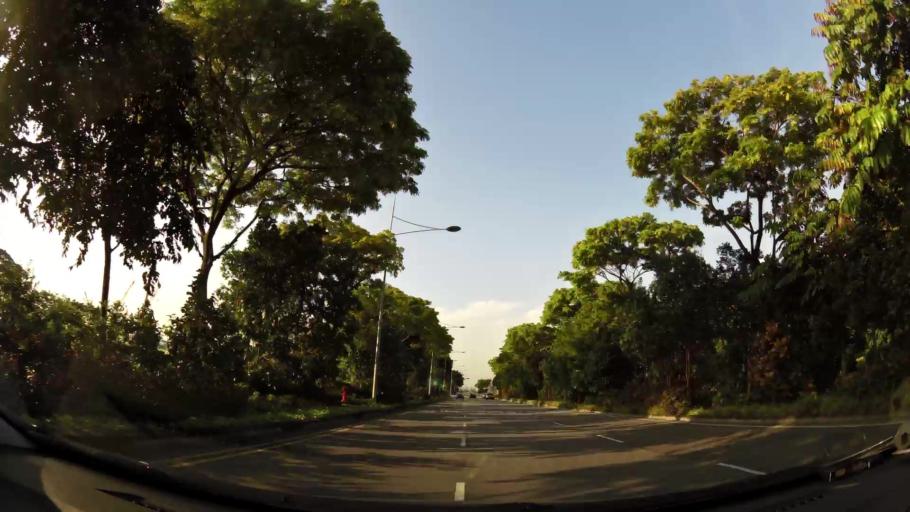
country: SG
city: Singapore
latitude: 1.2766
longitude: 103.8626
